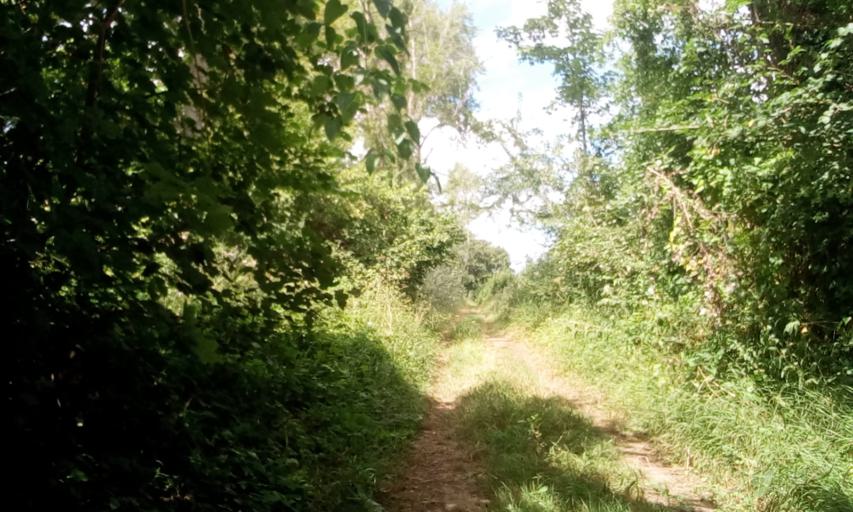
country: FR
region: Lower Normandy
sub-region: Departement du Calvados
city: Sannerville
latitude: 49.1553
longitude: -0.2062
